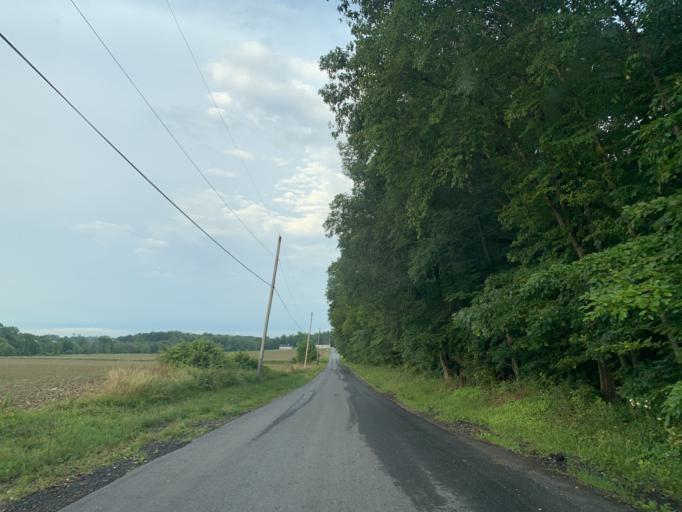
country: US
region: Maryland
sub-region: Cecil County
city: Rising Sun
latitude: 39.7217
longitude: -76.0199
